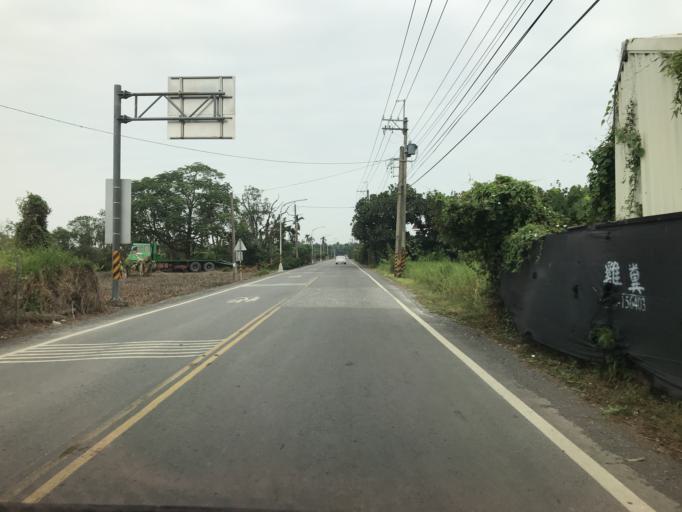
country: TW
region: Taiwan
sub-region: Pingtung
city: Pingtung
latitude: 22.4721
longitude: 120.6075
